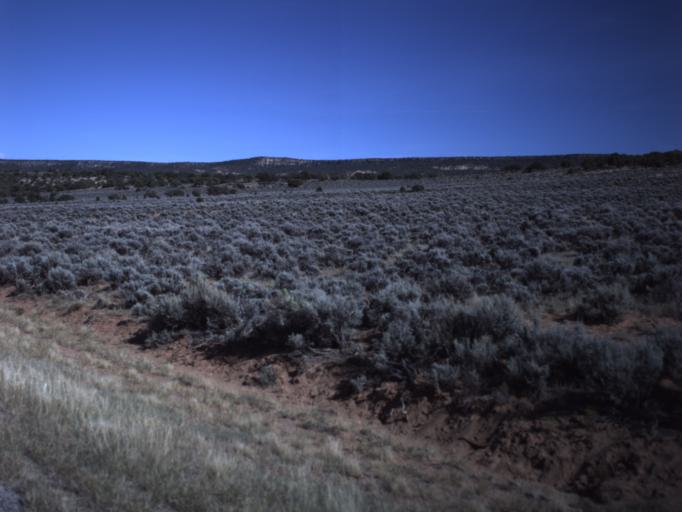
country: US
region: Utah
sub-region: San Juan County
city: Monticello
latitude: 37.9967
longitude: -109.4766
